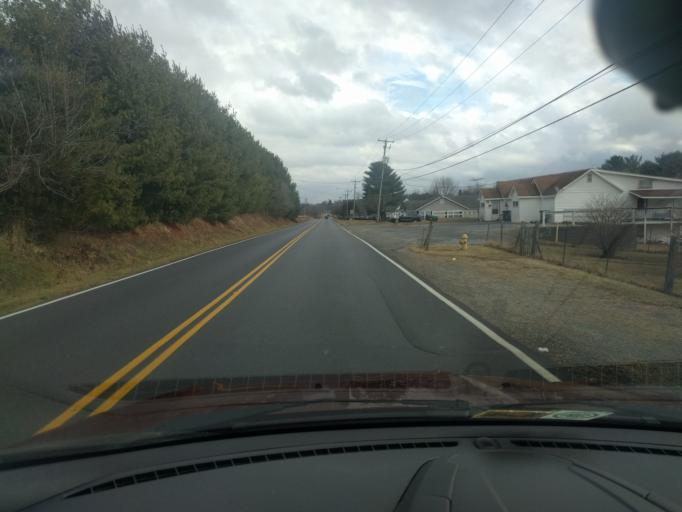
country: US
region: Virginia
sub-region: Pulaski County
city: Pulaski
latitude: 37.0621
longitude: -80.7339
